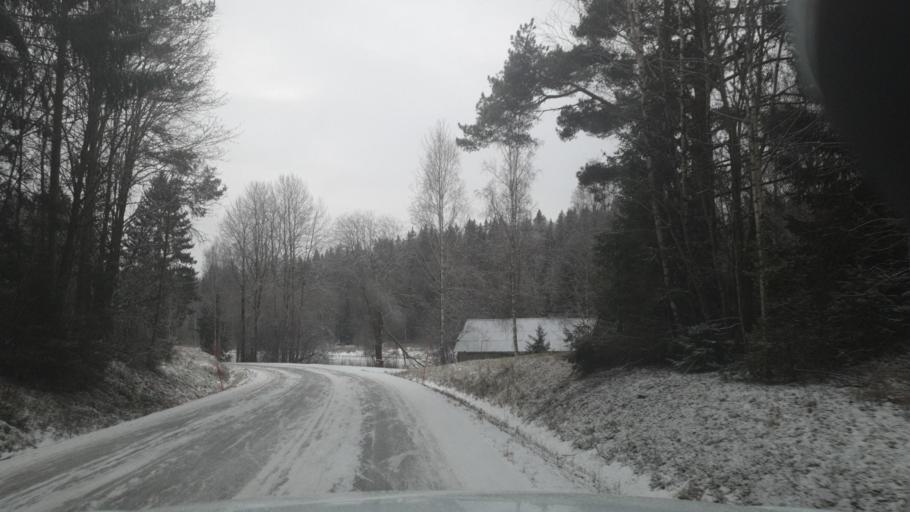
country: SE
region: Vaermland
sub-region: Arvika Kommun
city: Arvika
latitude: 59.6475
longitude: 12.8078
